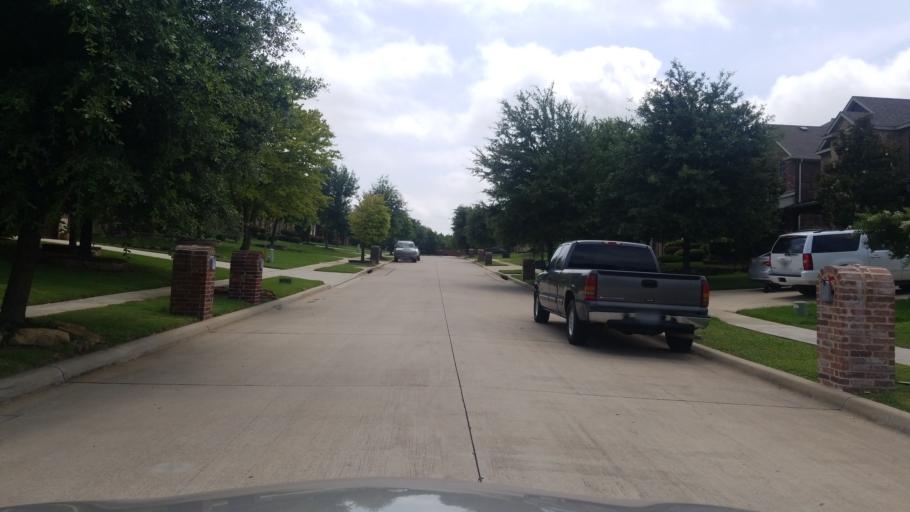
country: US
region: Texas
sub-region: Dallas County
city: Duncanville
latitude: 32.6845
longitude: -96.9372
